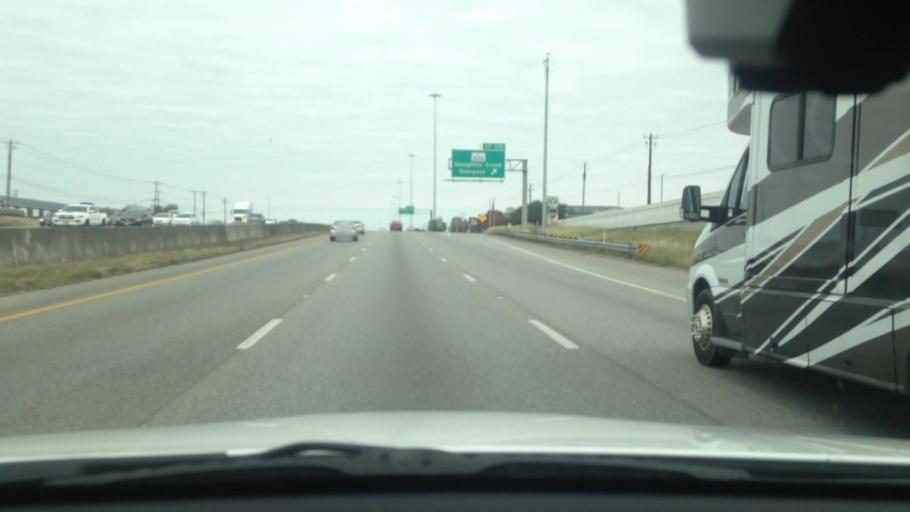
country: US
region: Texas
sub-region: Travis County
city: Onion Creek
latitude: 30.1377
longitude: -97.7969
